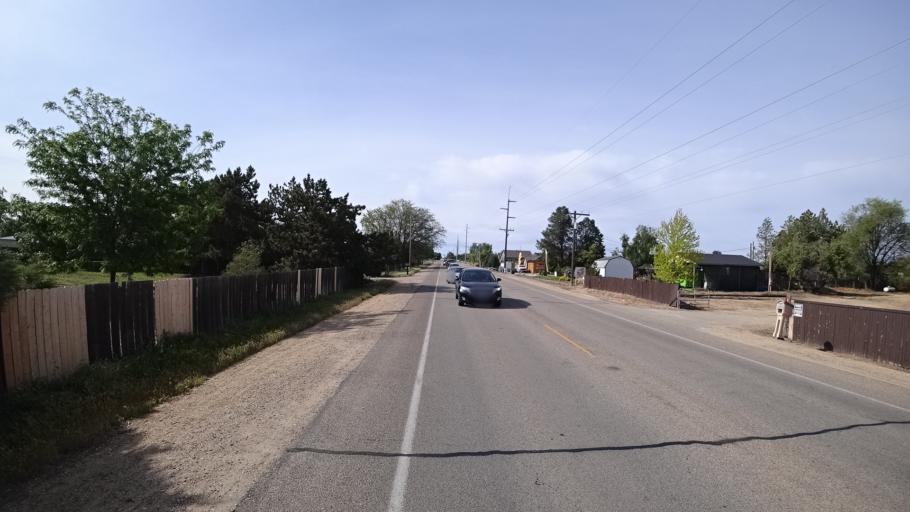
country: US
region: Idaho
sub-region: Ada County
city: Meridian
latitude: 43.5651
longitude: -116.3345
